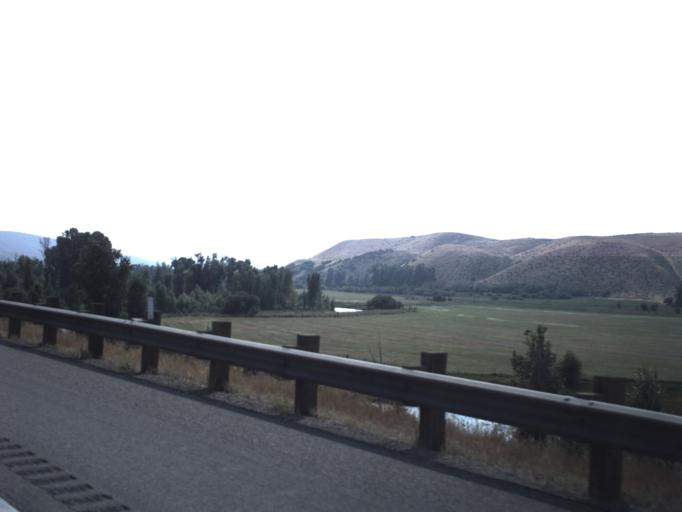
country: US
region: Utah
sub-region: Summit County
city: Coalville
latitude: 40.8482
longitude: -111.3893
